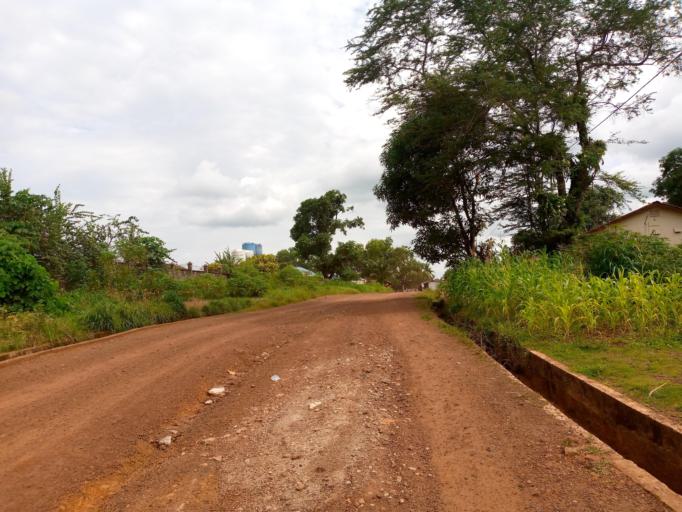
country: SL
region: Northern Province
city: Magburaka
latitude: 8.7219
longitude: -11.9392
